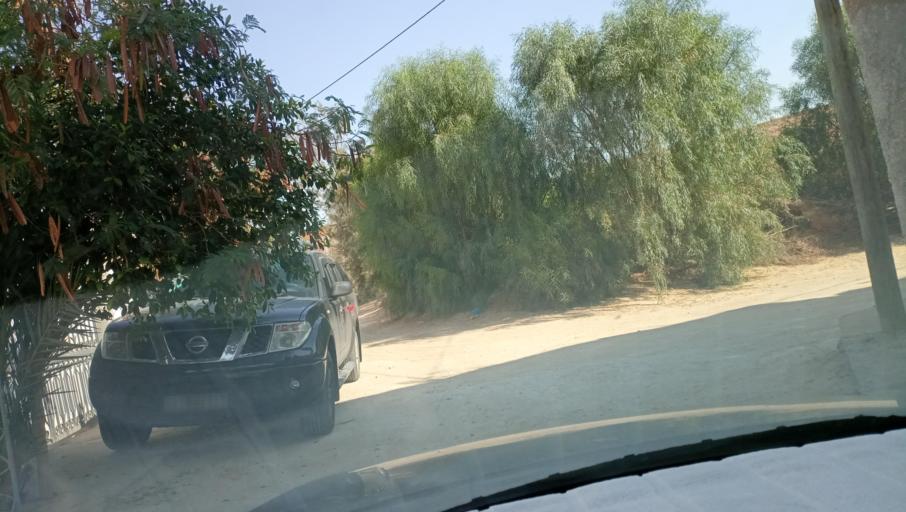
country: TN
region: Tataouine
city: Tataouine
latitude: 32.9820
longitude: 10.3817
